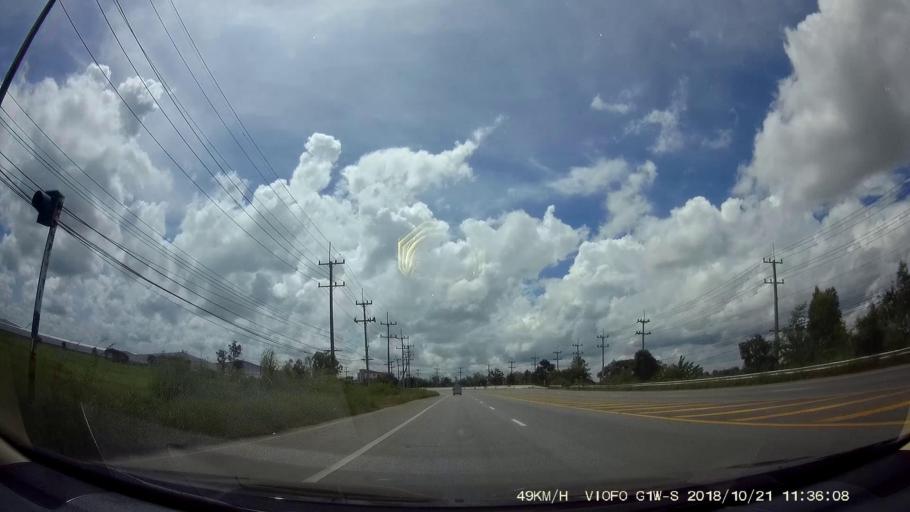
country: TH
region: Chaiyaphum
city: Chaiyaphum
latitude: 15.7221
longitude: 102.0171
